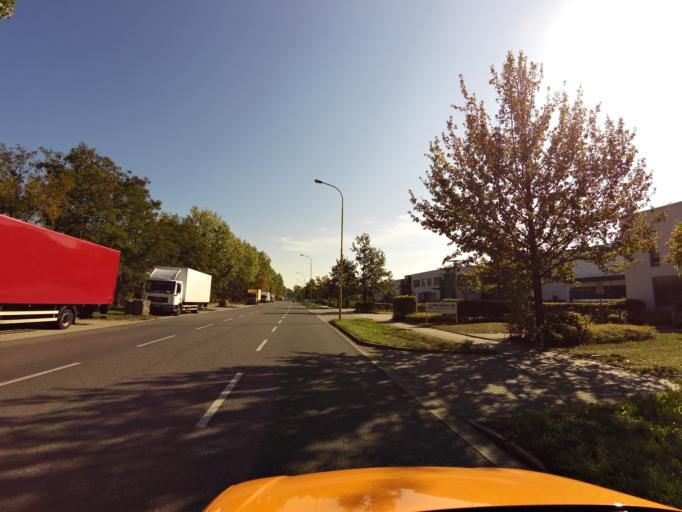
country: DE
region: Brandenburg
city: Grossbeeren
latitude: 52.3758
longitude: 13.3136
